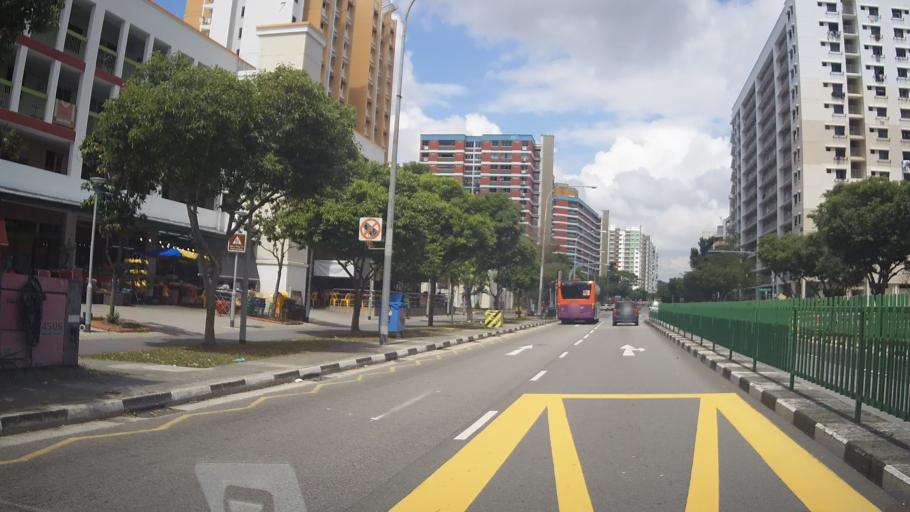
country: SG
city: Singapore
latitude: 1.3498
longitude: 103.9341
